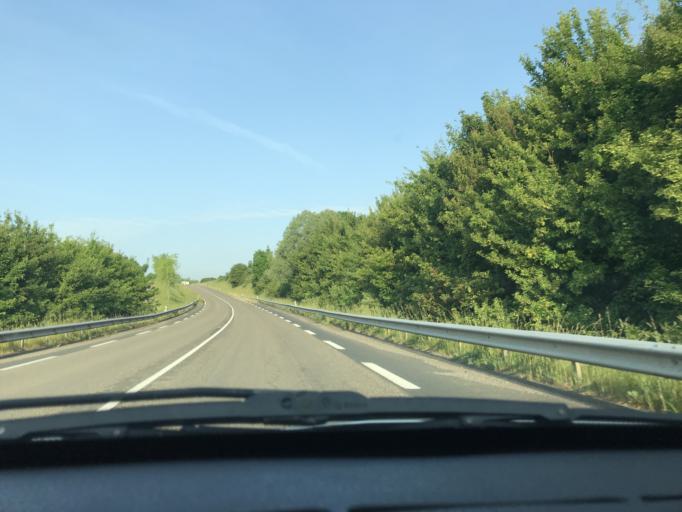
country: FR
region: Lorraine
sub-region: Departement de la Moselle
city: Vic-sur-Seille
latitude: 48.7764
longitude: 6.5410
